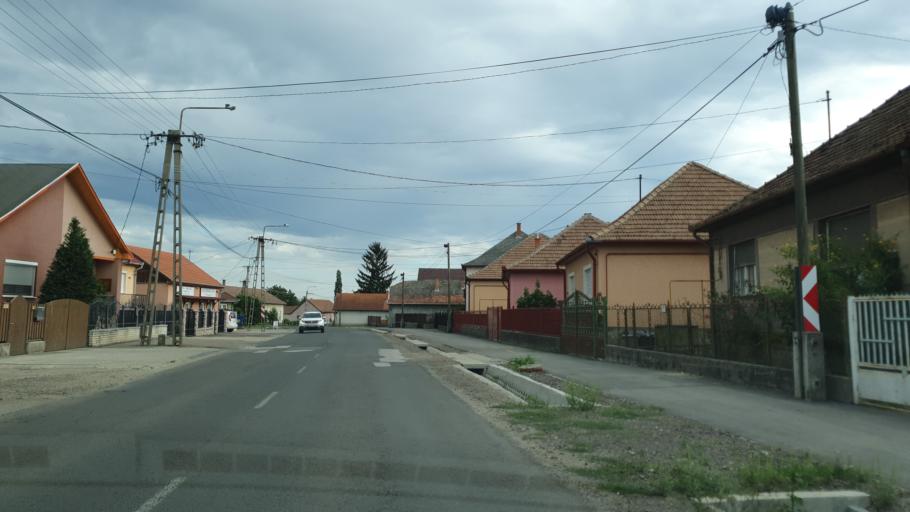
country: HU
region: Heves
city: Lorinci
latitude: 47.7527
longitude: 19.6792
